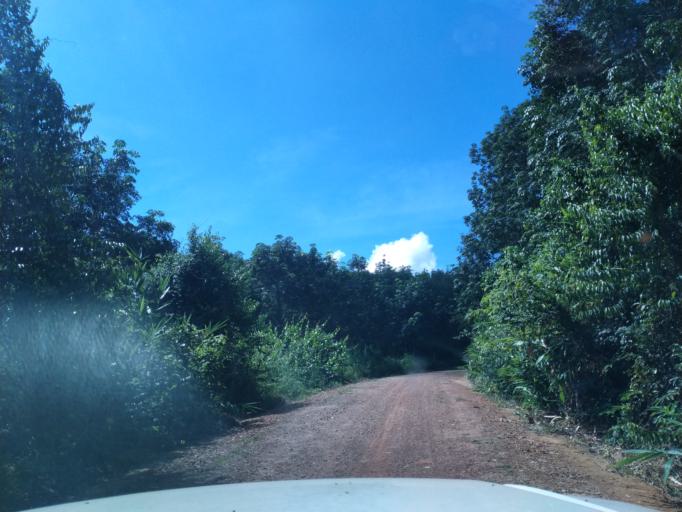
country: LA
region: Vientiane
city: Muang Phon-Hong
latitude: 18.6410
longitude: 102.8881
